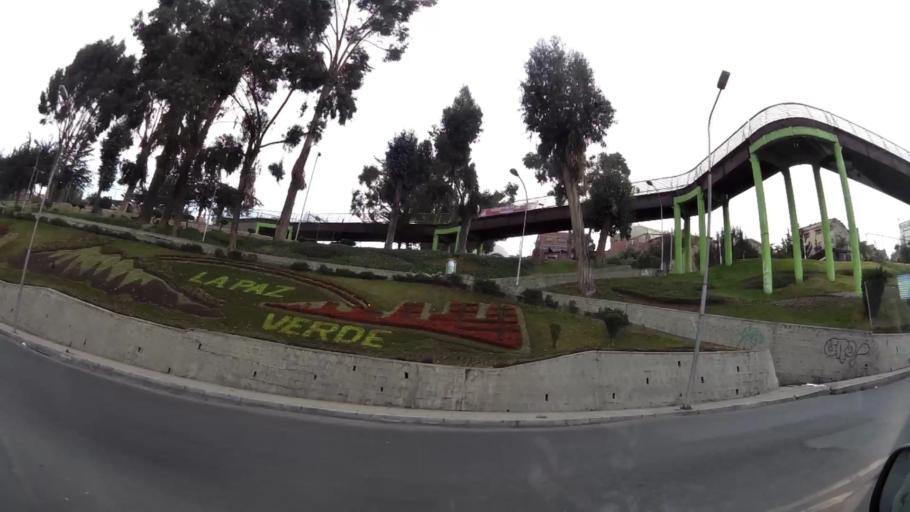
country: BO
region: La Paz
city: La Paz
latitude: -16.5018
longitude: -68.1278
